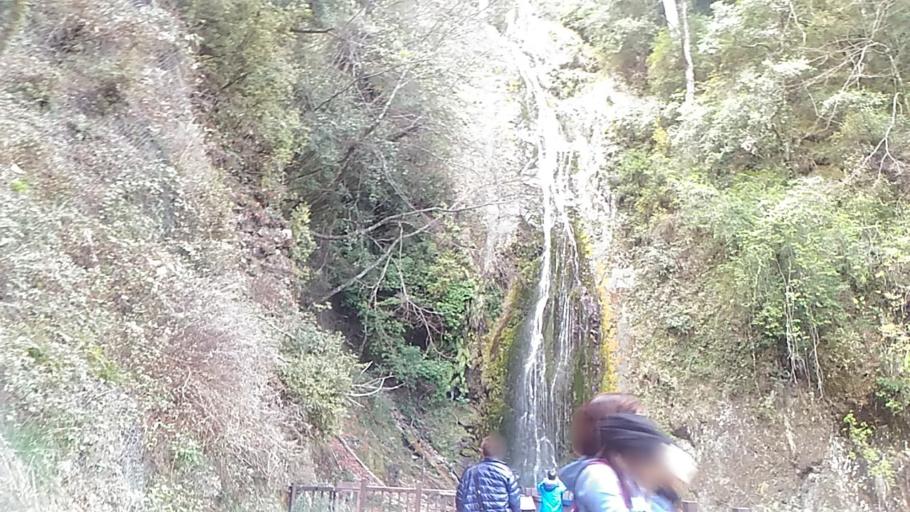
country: TW
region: Taiwan
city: Daxi
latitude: 24.4134
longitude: 121.3027
